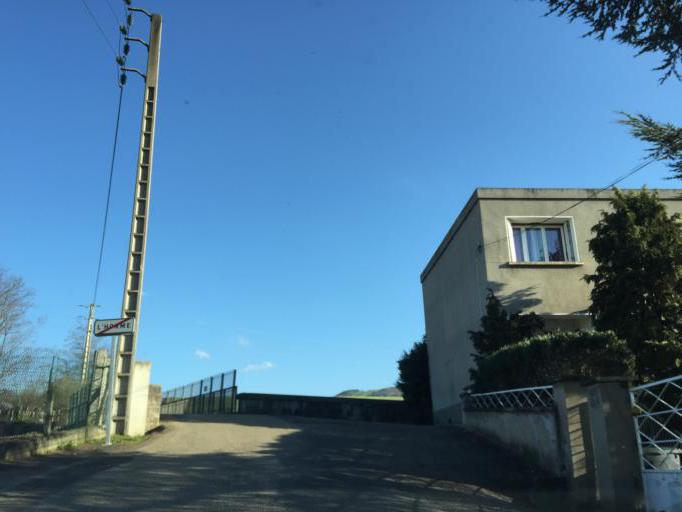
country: FR
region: Rhone-Alpes
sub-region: Departement de la Loire
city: La Grand-Croix
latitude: 45.4910
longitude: 4.5584
